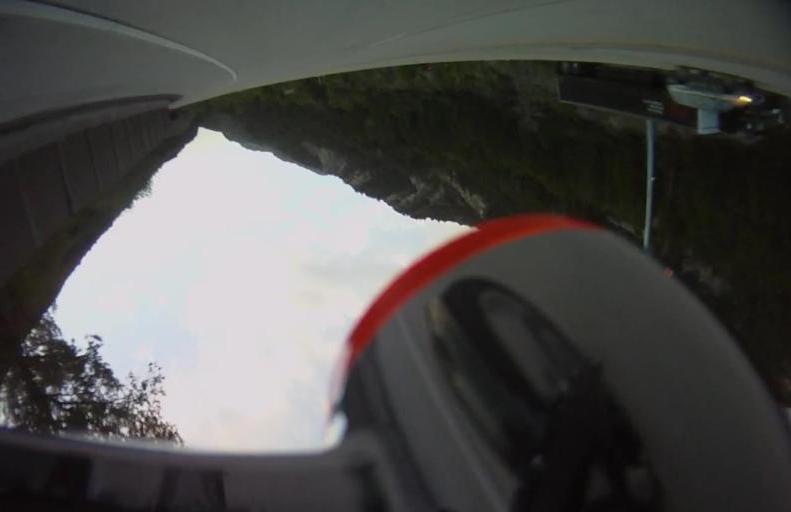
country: US
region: Utah
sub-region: Utah County
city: Orem
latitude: 40.3650
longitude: -111.5561
